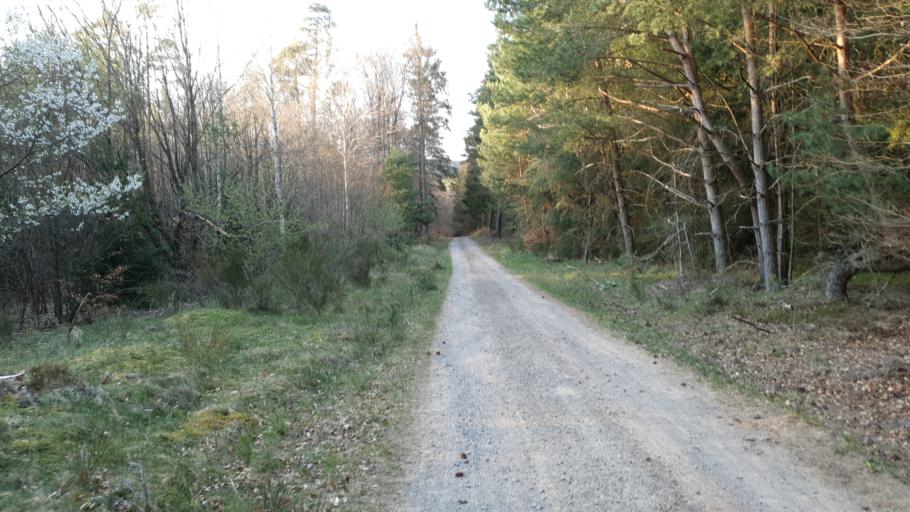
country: DE
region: Rheinland-Pfalz
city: Trippstadt
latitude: 49.3929
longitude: 7.8165
